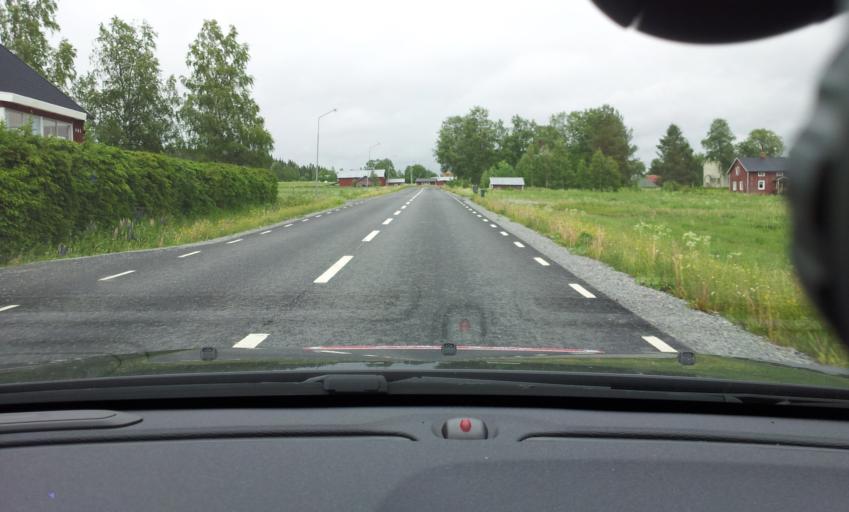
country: SE
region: Jaemtland
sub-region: OEstersunds Kommun
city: Lit
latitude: 63.7406
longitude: 14.8569
